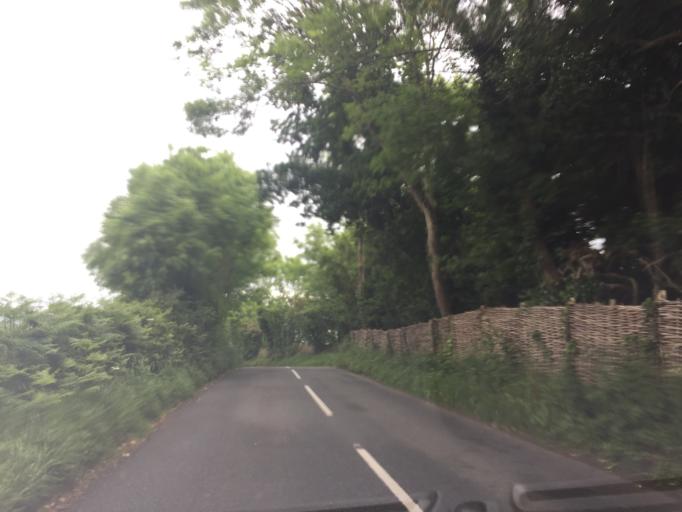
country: GB
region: England
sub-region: Dorset
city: Swanage
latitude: 50.6362
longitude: -1.9723
